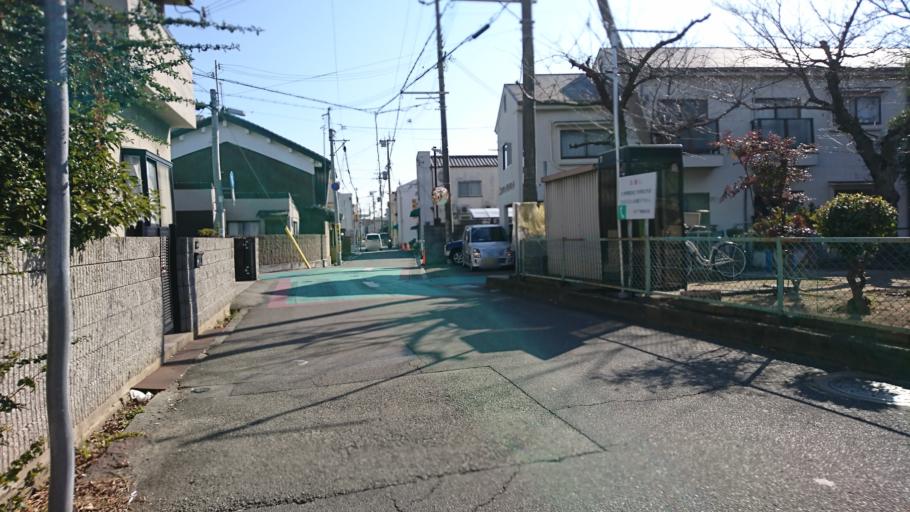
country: JP
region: Hyogo
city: Kakogawacho-honmachi
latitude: 34.7499
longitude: 134.7987
